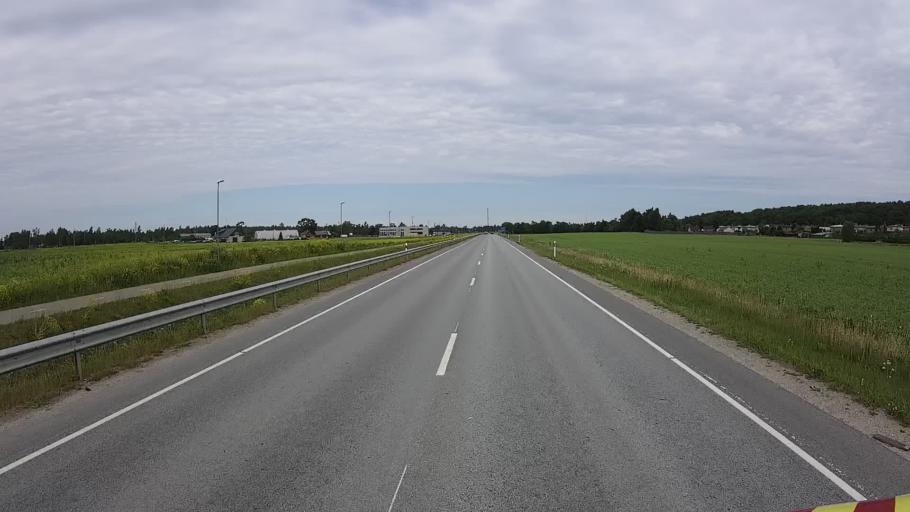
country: EE
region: Laeaene-Virumaa
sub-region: Rakvere linn
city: Rakvere
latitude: 59.3334
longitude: 26.3424
